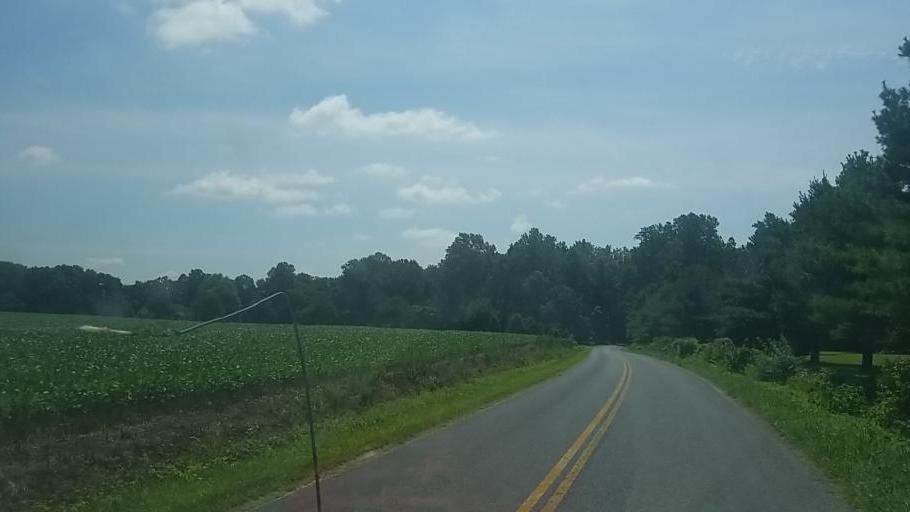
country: US
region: Maryland
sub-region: Caroline County
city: Ridgely
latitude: 38.9118
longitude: -75.9368
